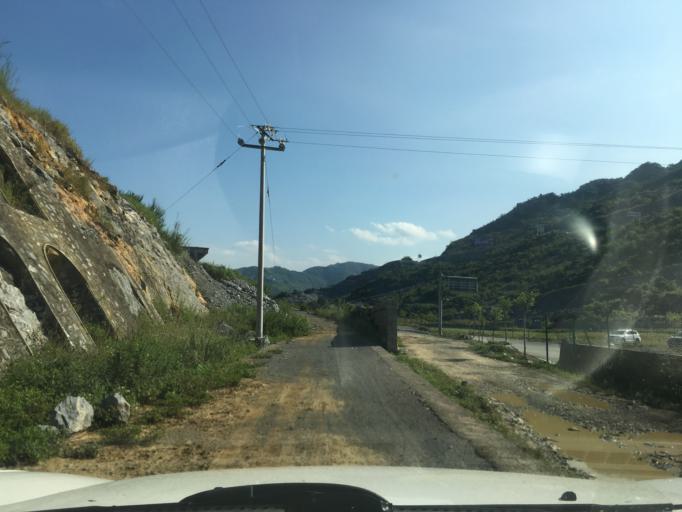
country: CN
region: Guangxi Zhuangzu Zizhiqu
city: Xinzhou
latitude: 25.4657
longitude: 105.7316
